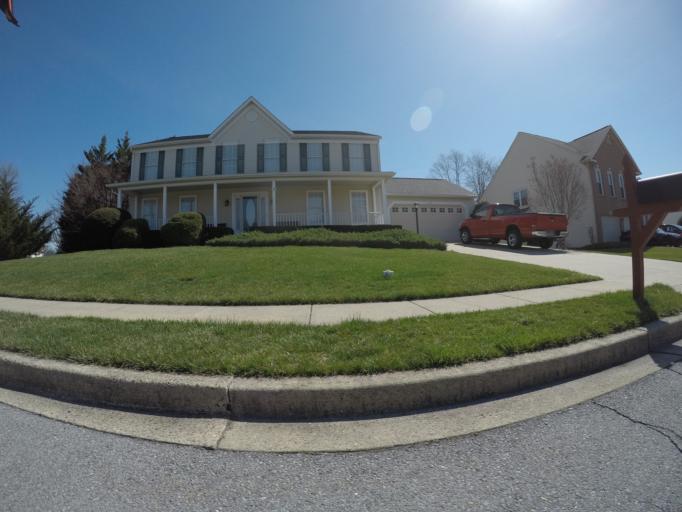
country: US
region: Maryland
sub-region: Frederick County
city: Ballenger Creek
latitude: 39.3811
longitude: -77.4268
